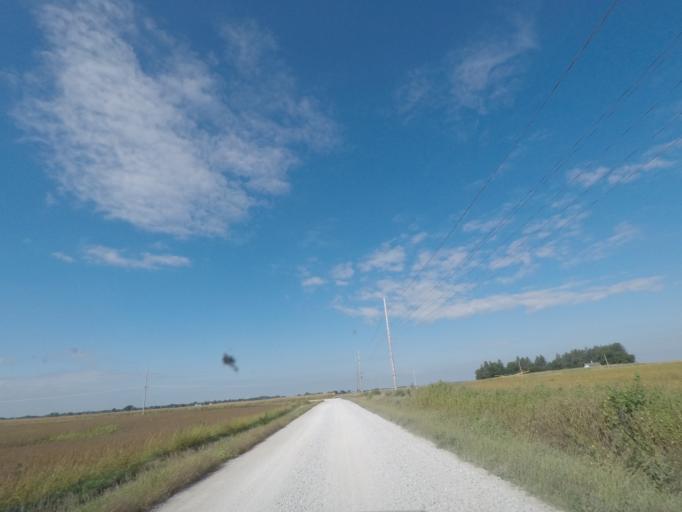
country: US
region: Iowa
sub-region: Story County
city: Nevada
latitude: 42.0345
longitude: -93.4234
